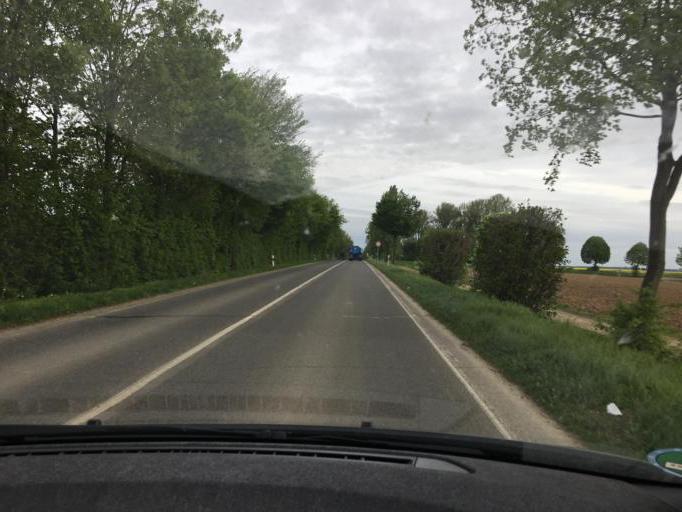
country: DE
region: North Rhine-Westphalia
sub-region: Regierungsbezirk Koln
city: Titz
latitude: 51.0550
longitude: 6.4286
